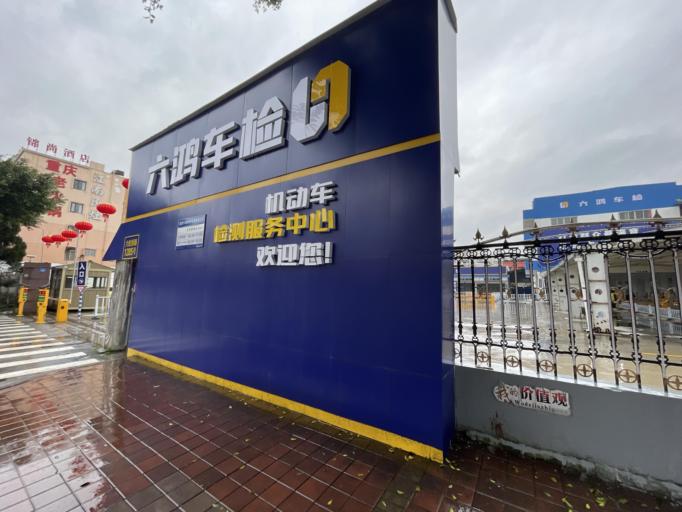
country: CN
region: Zhejiang Sheng
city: Louqiao
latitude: 27.9840
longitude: 120.6208
